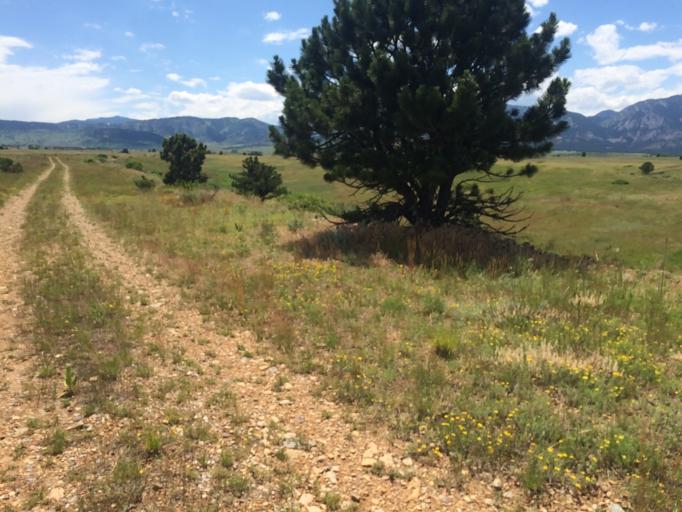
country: US
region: Colorado
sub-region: Boulder County
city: Superior
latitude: 39.9030
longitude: -105.2180
